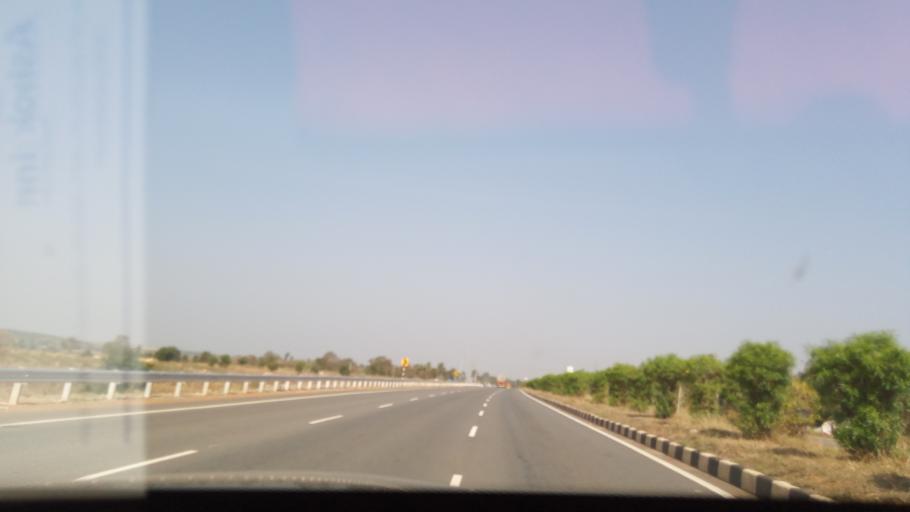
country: IN
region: Karnataka
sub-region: Haveri
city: Shiggaon
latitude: 15.0075
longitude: 75.2000
